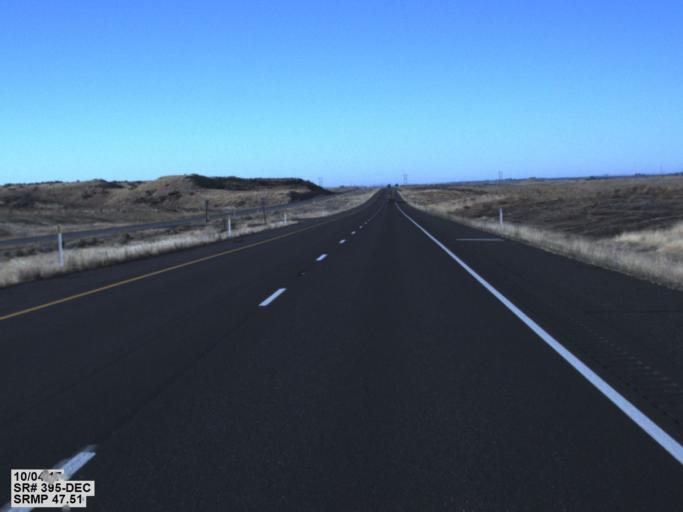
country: US
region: Washington
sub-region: Franklin County
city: Connell
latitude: 46.5839
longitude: -118.9694
